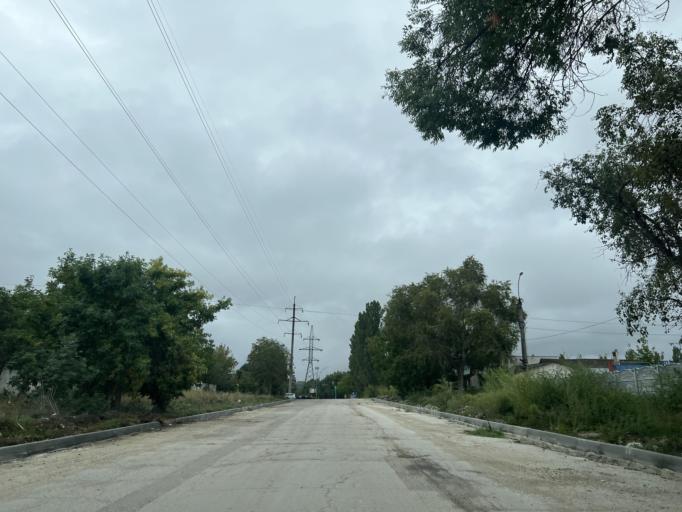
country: MD
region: Ungheni
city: Ungheni
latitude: 47.2236
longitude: 27.8075
